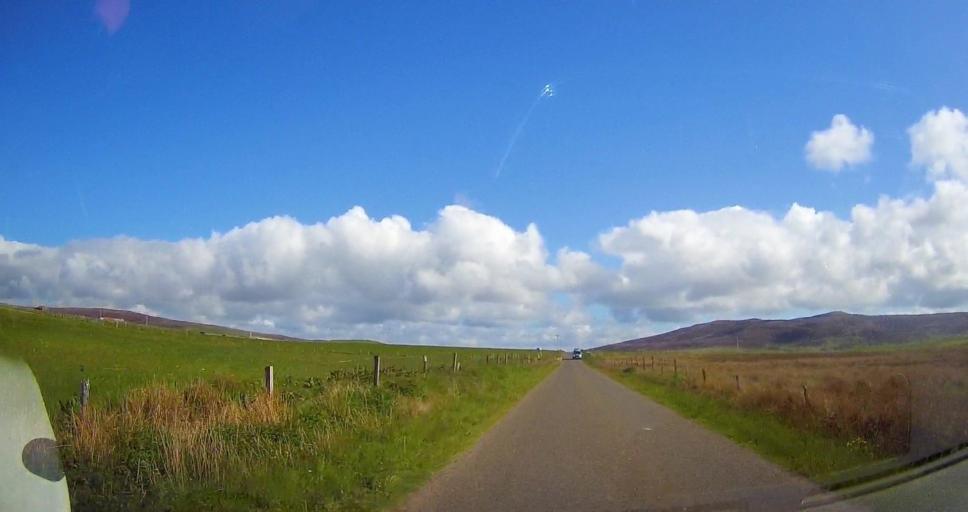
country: GB
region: Scotland
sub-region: Orkney Islands
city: Stromness
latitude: 58.9923
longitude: -3.1569
